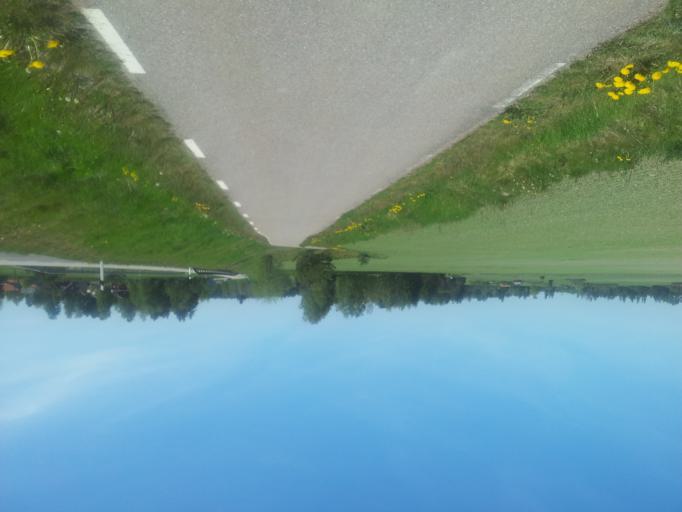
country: SE
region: Uppsala
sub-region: Uppsala Kommun
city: Saevja
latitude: 59.8564
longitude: 17.8040
